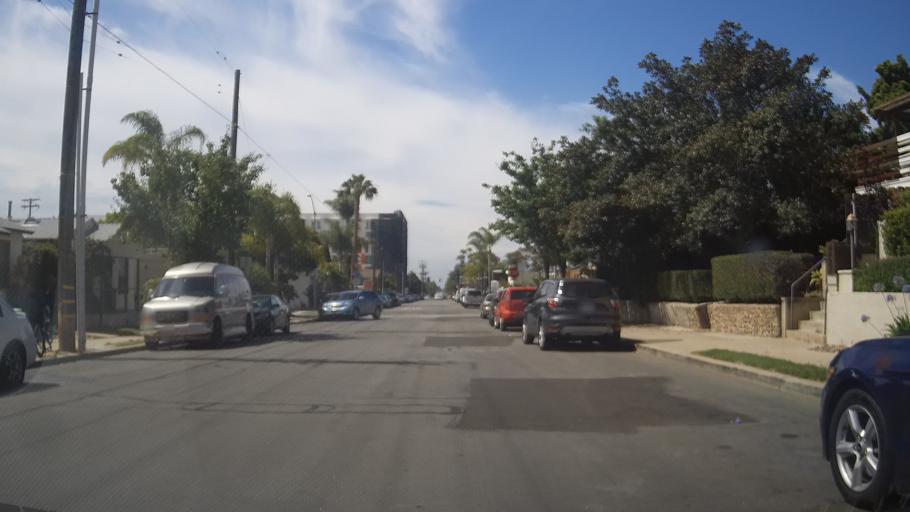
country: US
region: California
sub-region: San Diego County
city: San Diego
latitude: 32.7579
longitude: -117.1438
